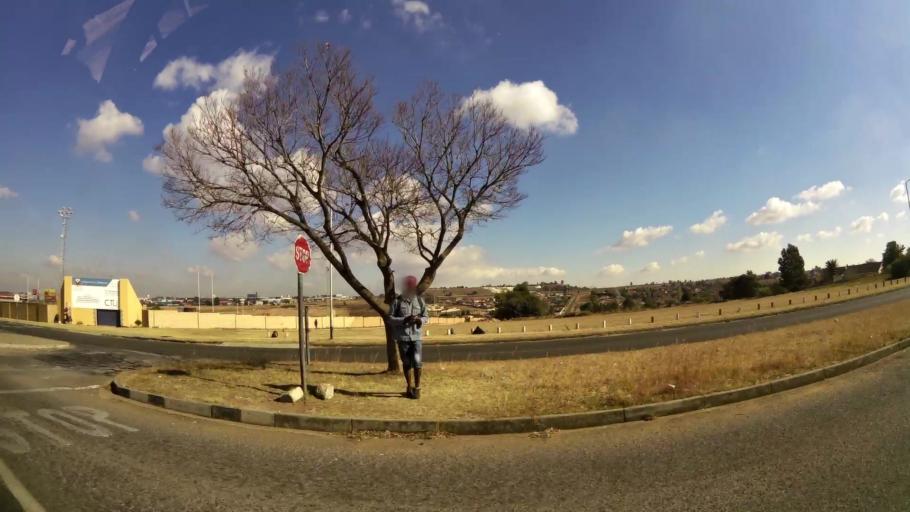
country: ZA
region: Gauteng
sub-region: City of Johannesburg Metropolitan Municipality
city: Roodepoort
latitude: -26.1471
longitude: 27.8240
